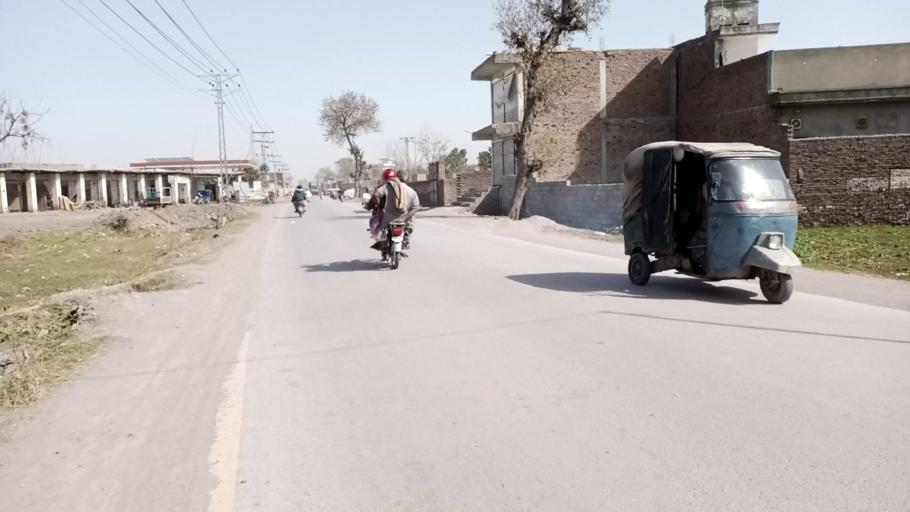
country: PK
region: Khyber Pakhtunkhwa
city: Peshawar
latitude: 34.0010
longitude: 71.6369
